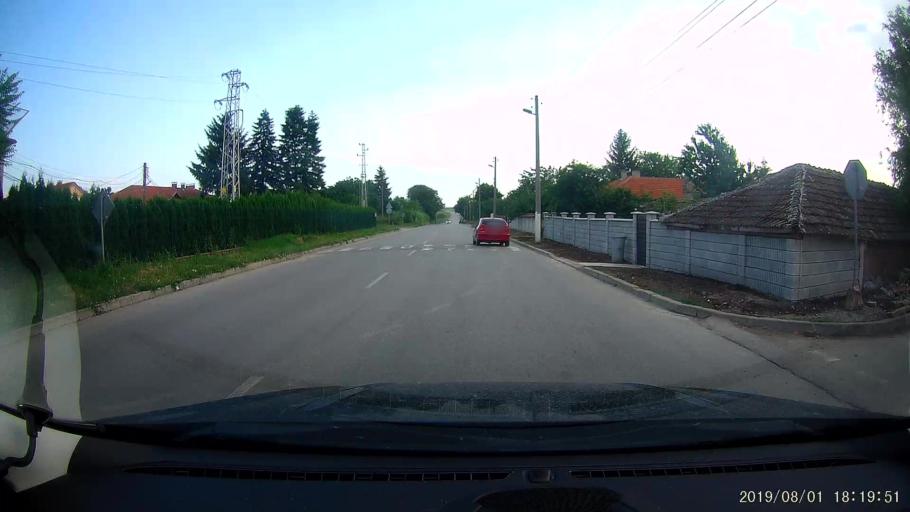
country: BG
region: Shumen
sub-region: Obshtina Kaolinovo
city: Kaolinovo
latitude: 43.6798
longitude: 27.0907
